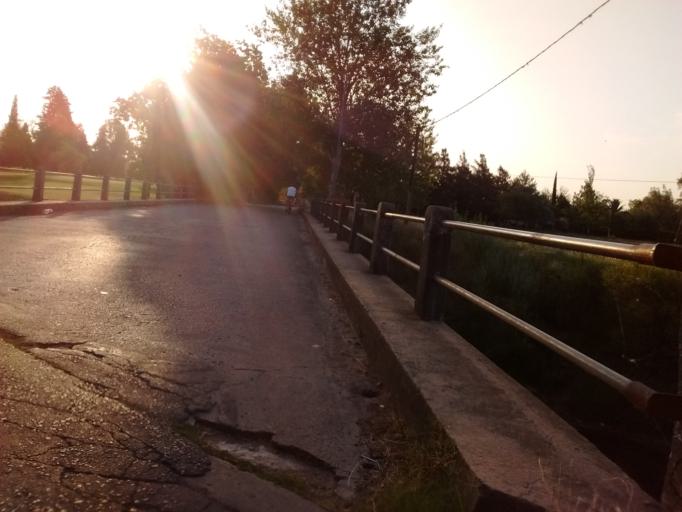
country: AR
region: Santa Fe
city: Funes
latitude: -32.9198
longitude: -60.7577
